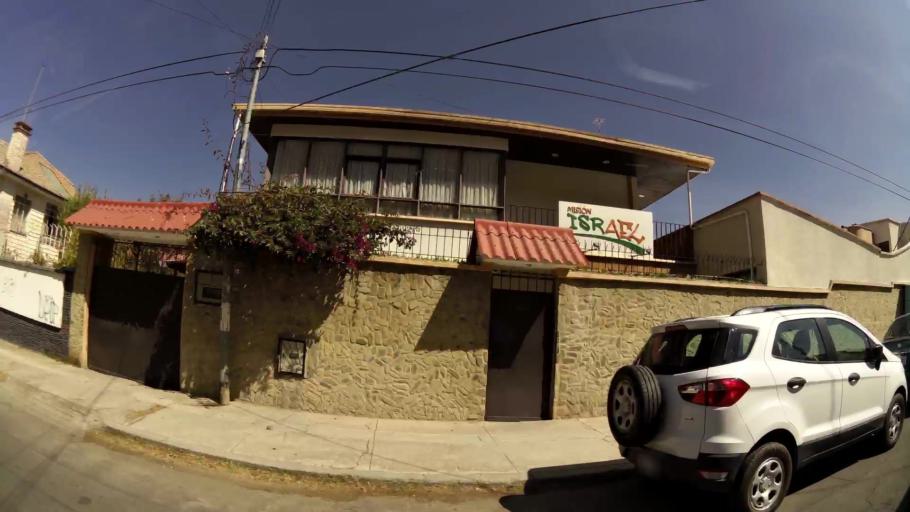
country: BO
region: La Paz
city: La Paz
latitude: -16.5275
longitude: -68.0843
